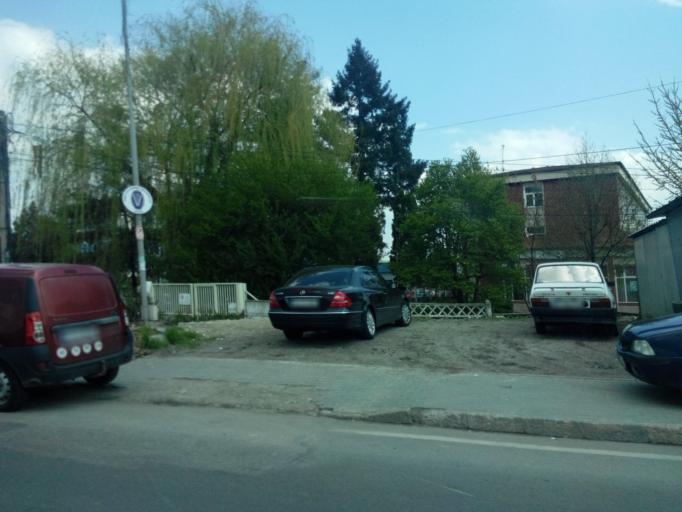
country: RO
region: Arges
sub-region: Comuna Albestii de Arges
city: Pitesti
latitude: 44.8691
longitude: 24.8837
